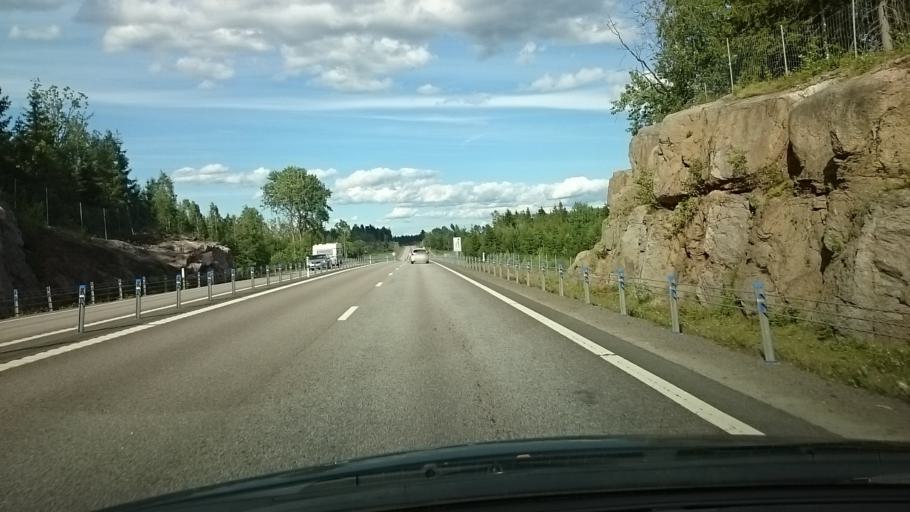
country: SE
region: OErebro
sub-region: Askersunds Kommun
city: Askersund
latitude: 58.8159
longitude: 14.8638
